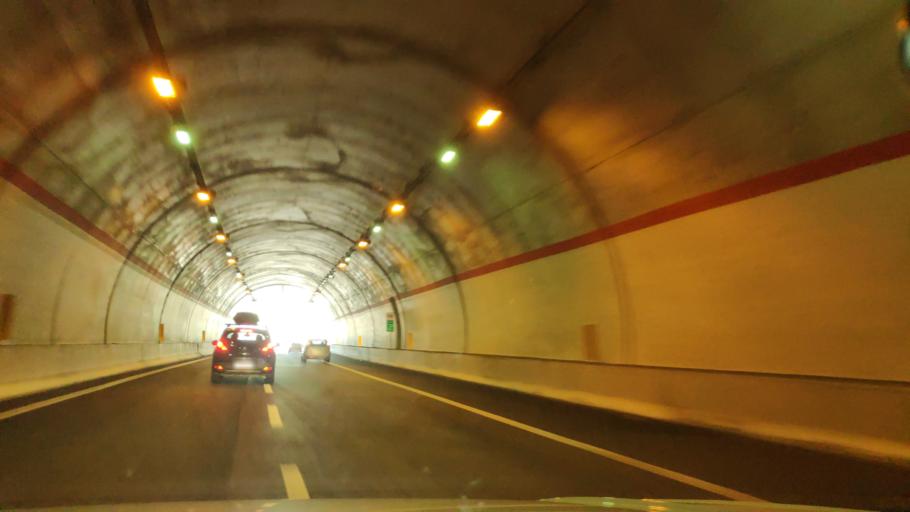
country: IT
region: Calabria
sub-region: Provincia di Cosenza
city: Morano Calabro
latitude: 39.8665
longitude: 16.0803
